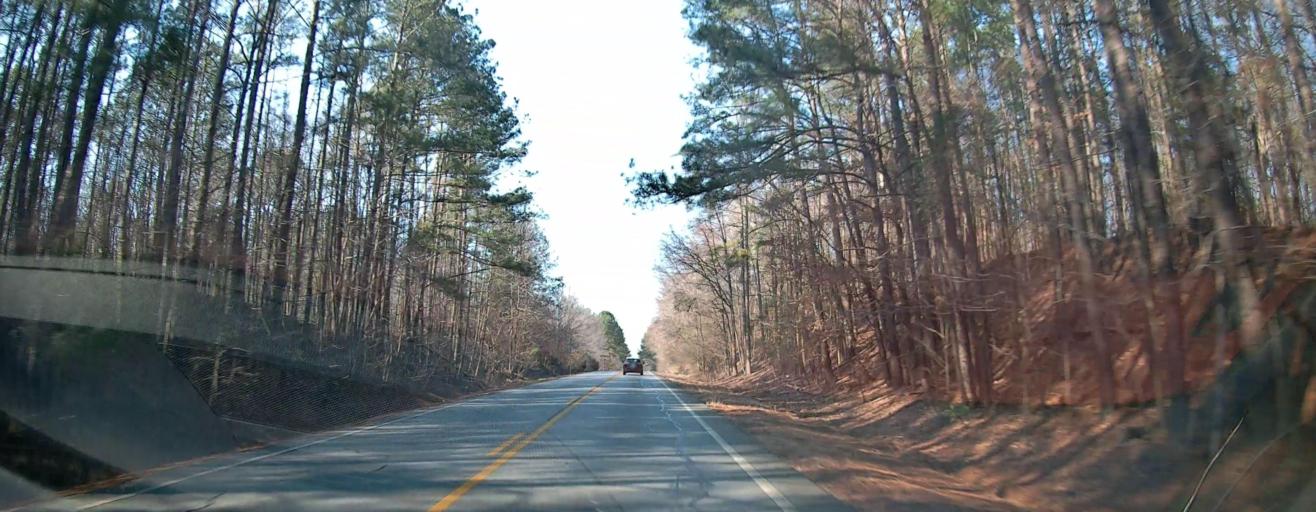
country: US
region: Georgia
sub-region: Butts County
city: Indian Springs
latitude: 33.2048
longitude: -83.8568
